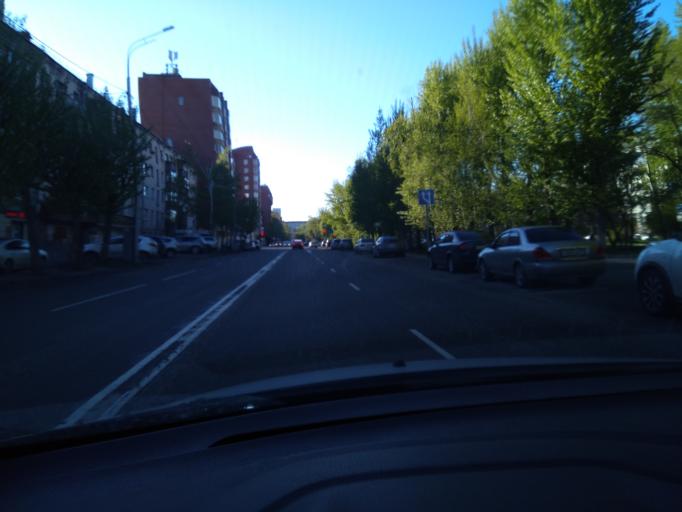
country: RU
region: Tjumen
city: Tyumen
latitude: 57.1331
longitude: 65.5844
